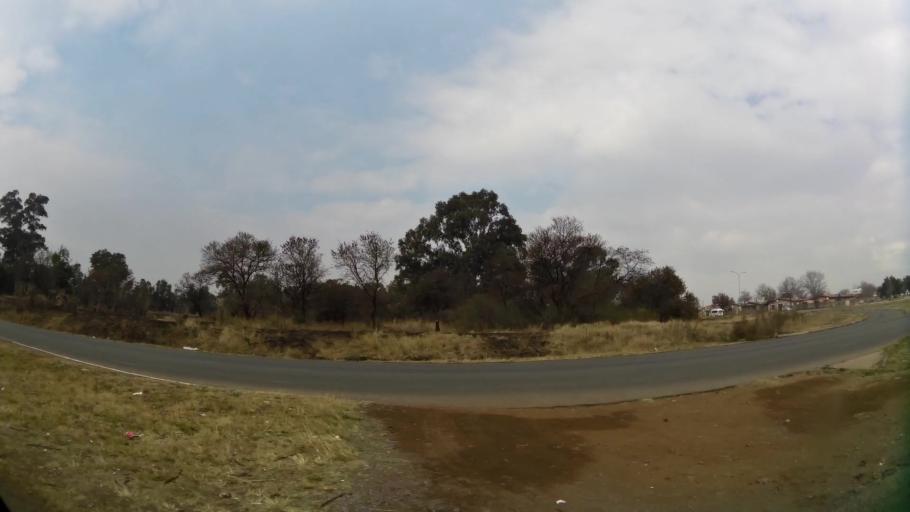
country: ZA
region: Gauteng
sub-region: Sedibeng District Municipality
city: Vanderbijlpark
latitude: -26.6739
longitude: 27.8382
